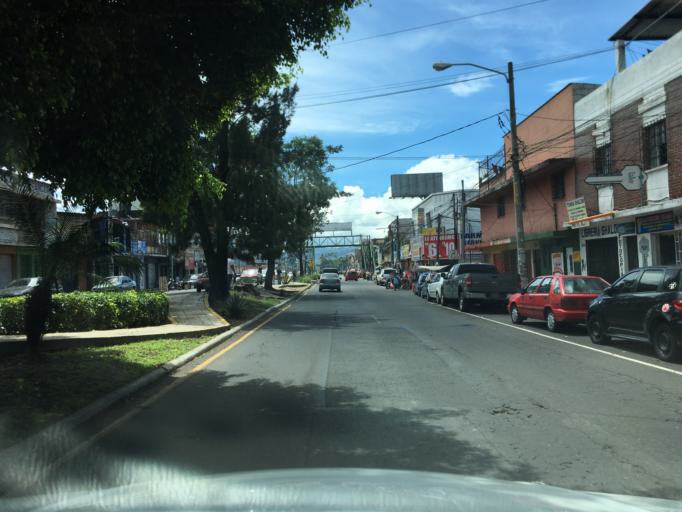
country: GT
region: Guatemala
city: Guatemala City
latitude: 14.6267
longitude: -90.5435
